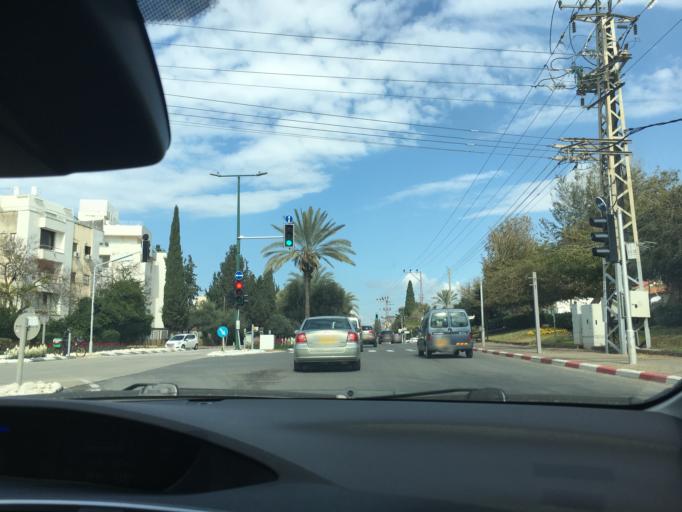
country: IL
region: Tel Aviv
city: Ramat HaSharon
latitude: 32.1676
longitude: 34.8529
